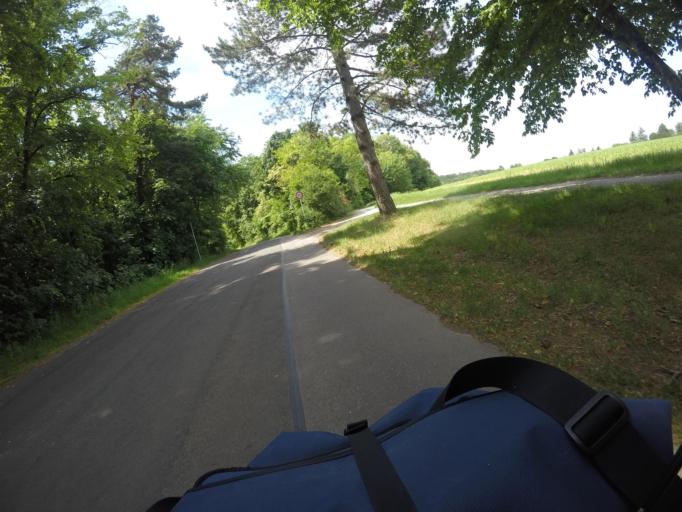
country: DE
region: Baden-Wuerttemberg
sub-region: Karlsruhe Region
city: Weingarten
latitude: 48.9923
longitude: 8.4969
